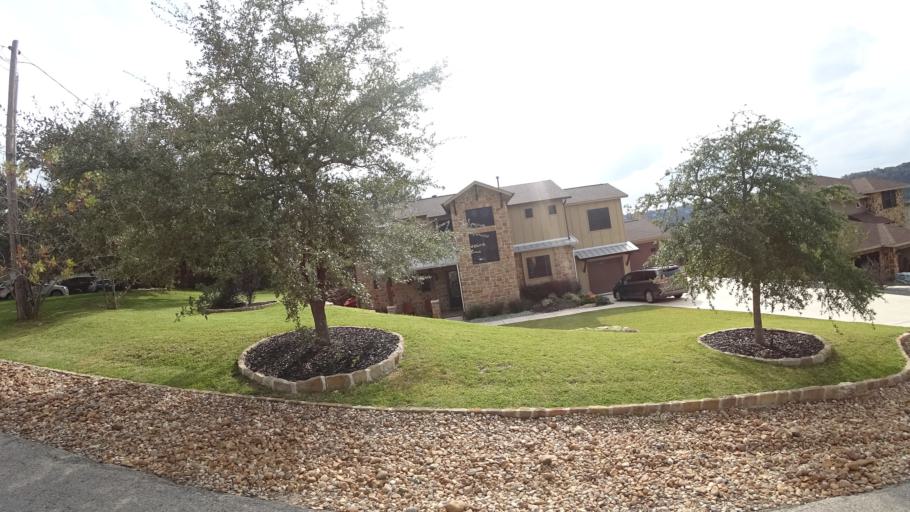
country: US
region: Texas
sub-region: Travis County
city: Hudson Bend
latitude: 30.3822
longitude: -97.9072
